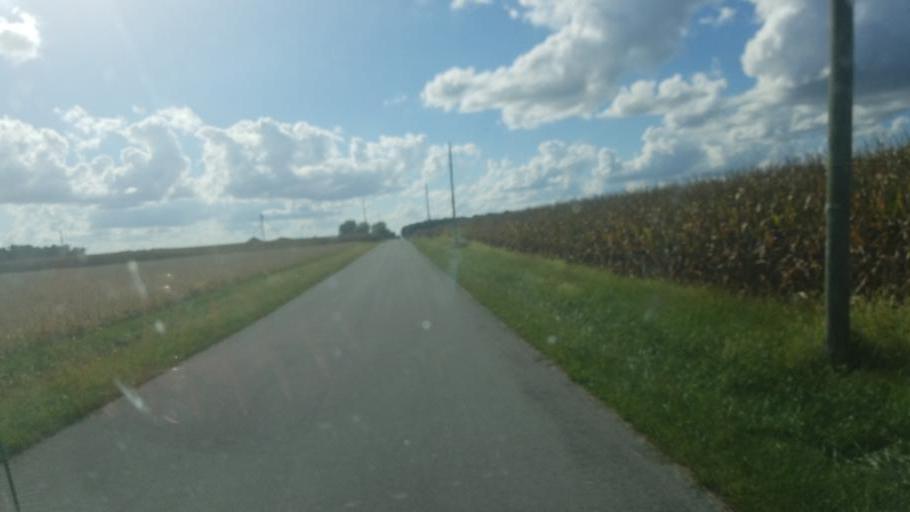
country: US
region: Ohio
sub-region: Hardin County
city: Kenton
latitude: 40.7182
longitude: -83.7089
